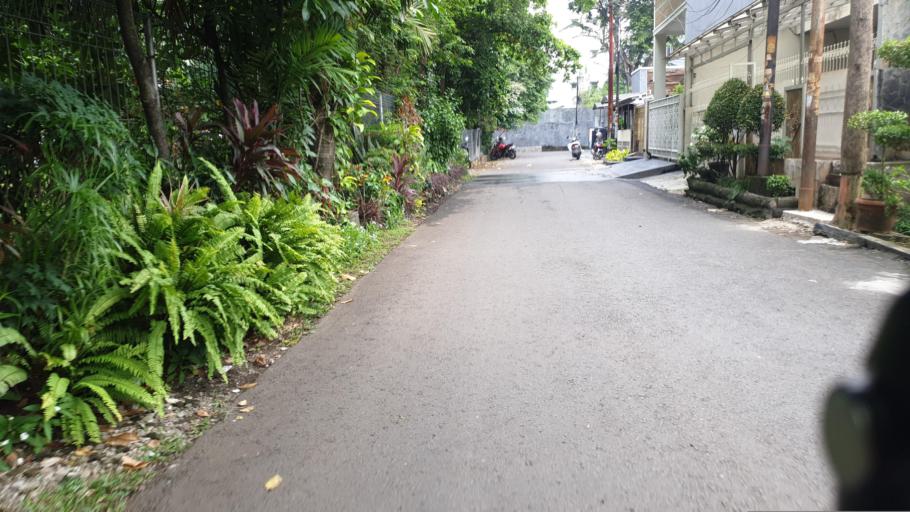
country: ID
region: West Java
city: Ciputat
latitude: -6.1937
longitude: 106.7545
